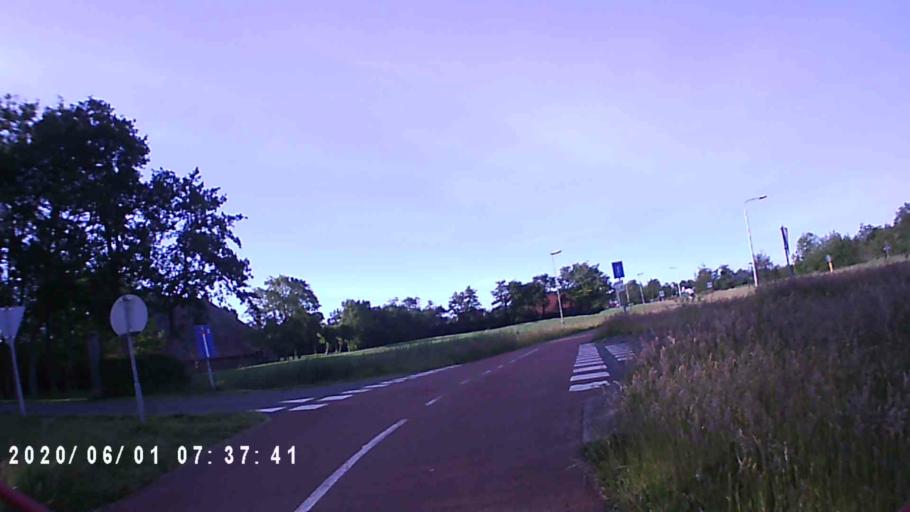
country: NL
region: Friesland
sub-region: Gemeente Dantumadiel
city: Damwald
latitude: 53.2978
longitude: 5.9964
